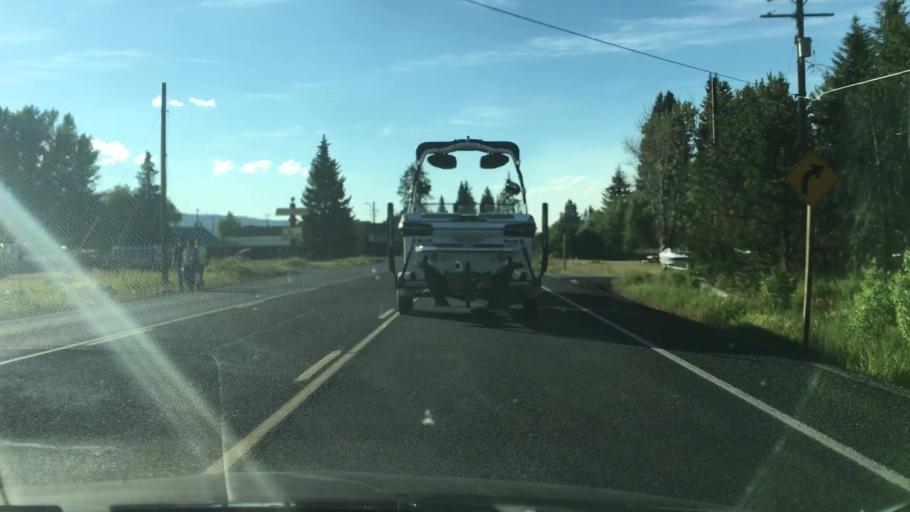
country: US
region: Idaho
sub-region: Valley County
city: McCall
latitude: 44.7293
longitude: -116.0769
